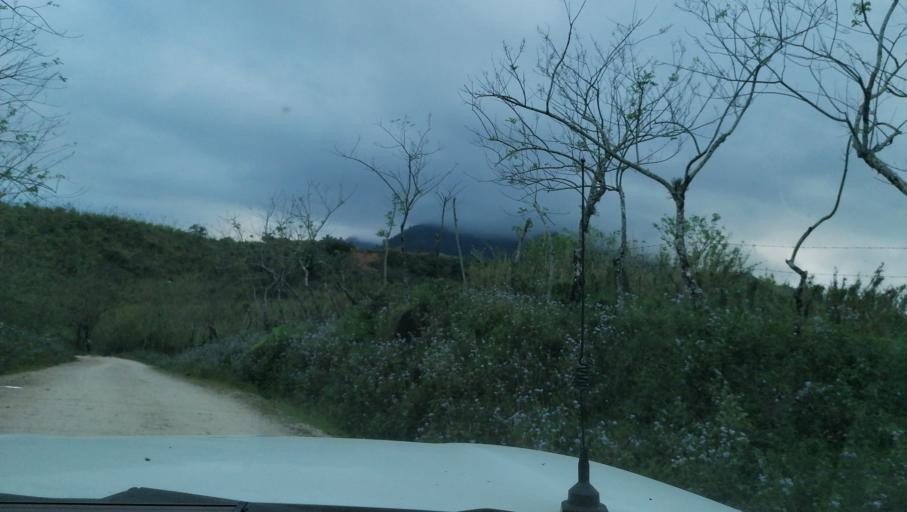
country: MX
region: Chiapas
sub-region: Francisco Leon
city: San Miguel la Sardina
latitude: 17.2909
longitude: -93.2709
